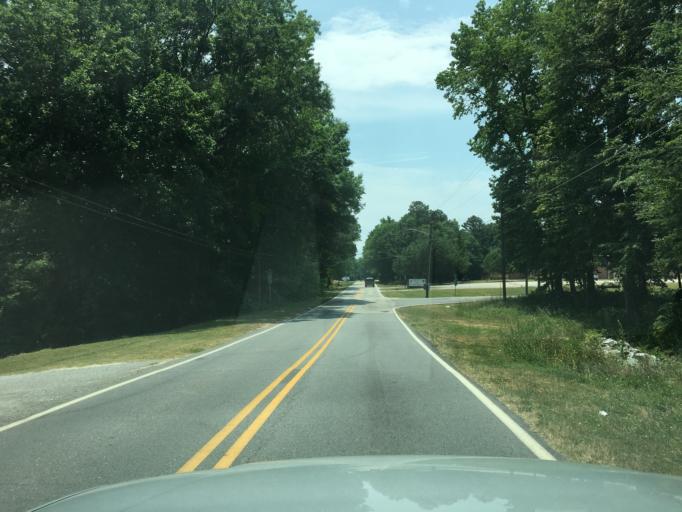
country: US
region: Georgia
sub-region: Hart County
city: Hartwell
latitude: 34.3476
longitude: -82.9191
